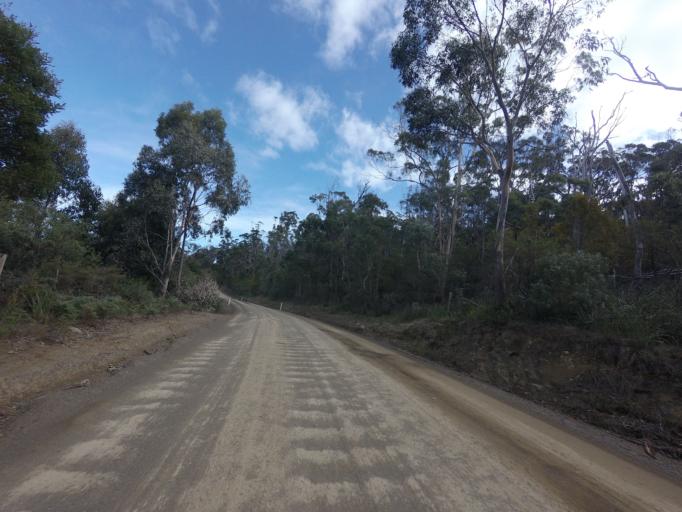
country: AU
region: Tasmania
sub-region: Clarence
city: Sandford
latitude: -43.0935
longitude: 147.7263
